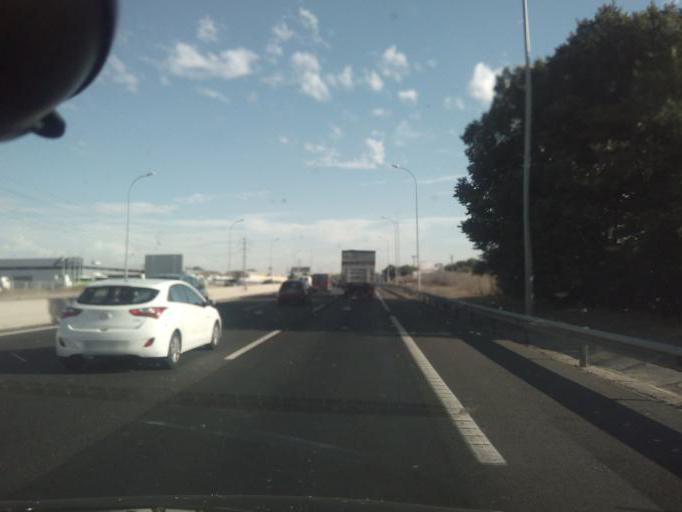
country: ES
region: Madrid
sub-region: Provincia de Madrid
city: Pinto
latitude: 40.2605
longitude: -3.6904
